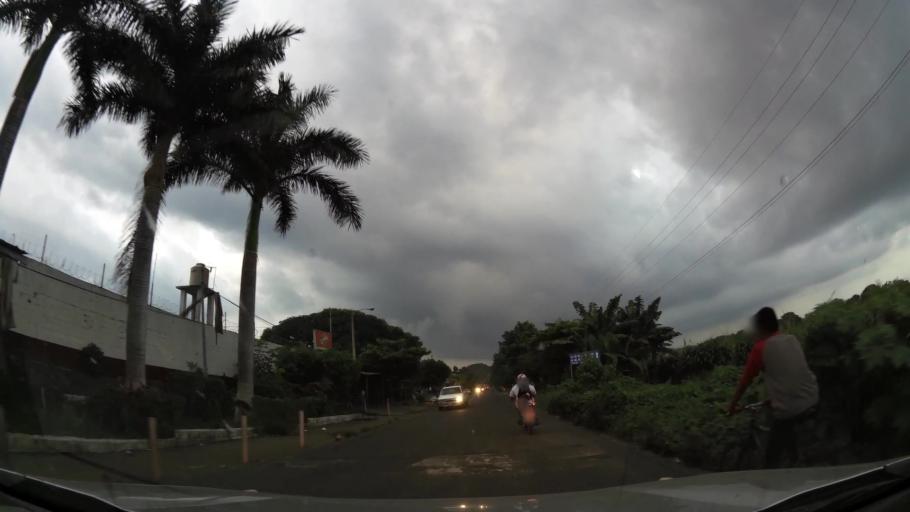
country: GT
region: Escuintla
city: Santa Lucia Cotzumalguapa
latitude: 14.3180
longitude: -91.0391
